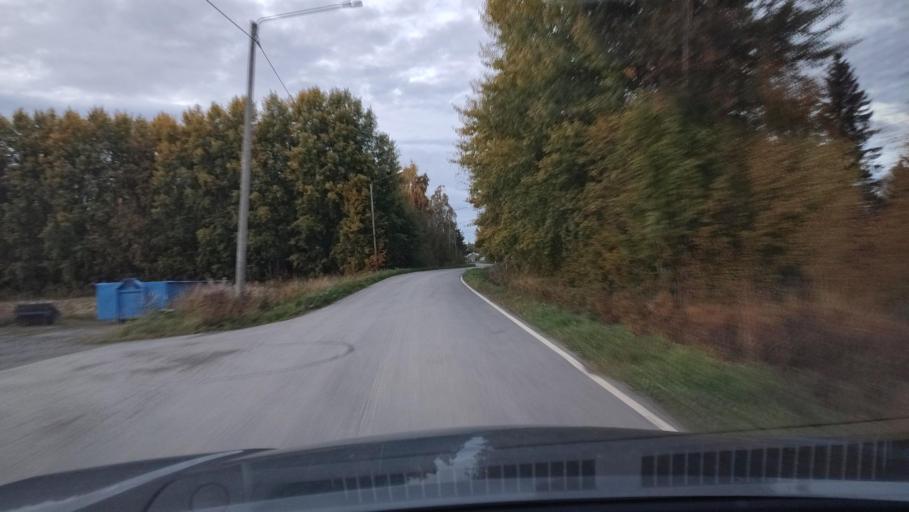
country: FI
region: Ostrobothnia
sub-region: Sydosterbotten
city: Kristinestad
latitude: 62.2660
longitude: 21.5092
